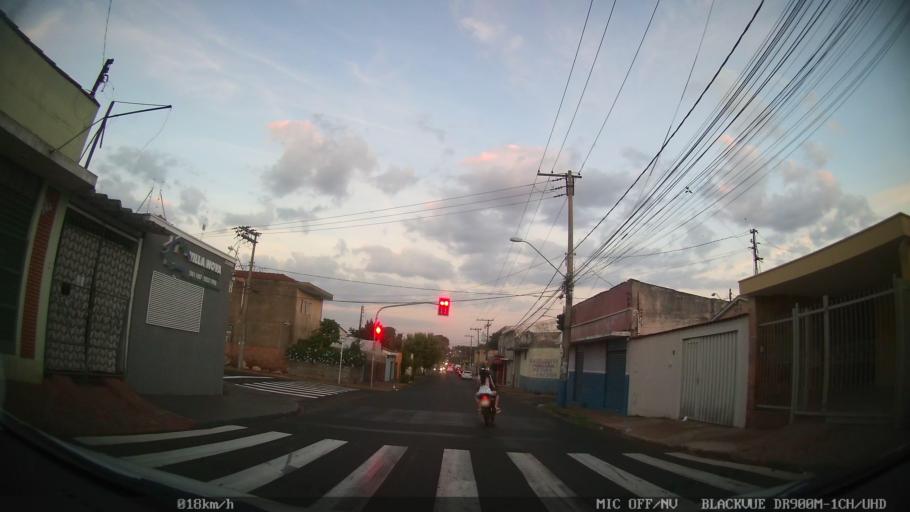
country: BR
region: Sao Paulo
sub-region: Ribeirao Preto
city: Ribeirao Preto
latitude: -21.1522
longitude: -47.8109
